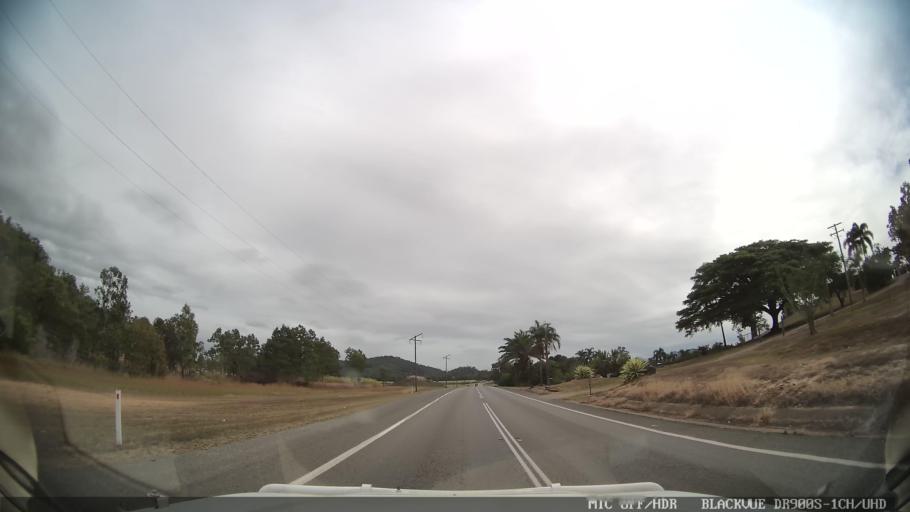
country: AU
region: Queensland
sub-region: Hinchinbrook
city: Ingham
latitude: -18.8585
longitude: 146.1652
